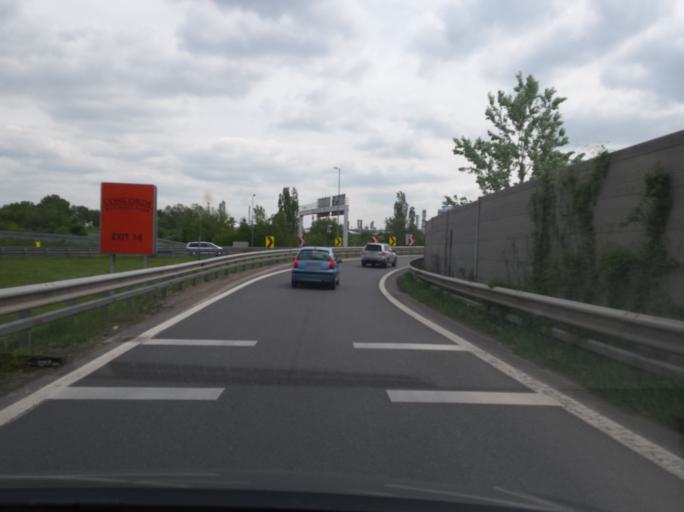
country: AT
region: Lower Austria
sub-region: Politischer Bezirk Wien-Umgebung
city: Schwechat
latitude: 48.1499
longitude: 16.4877
